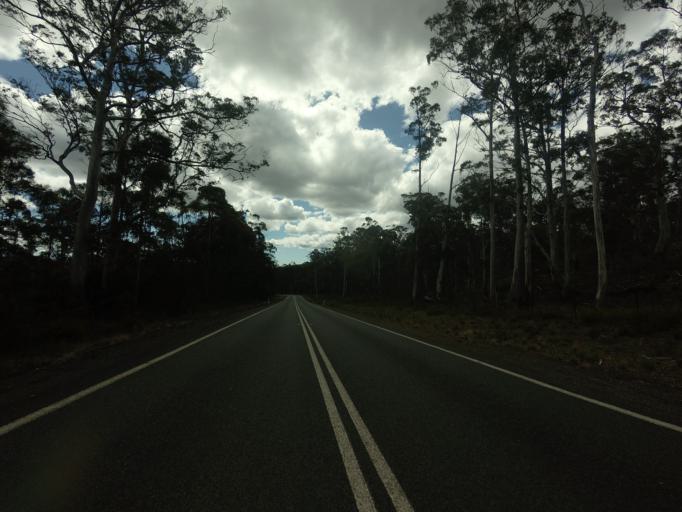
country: AU
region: Tasmania
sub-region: Northern Midlands
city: Evandale
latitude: -41.9941
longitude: 147.7145
